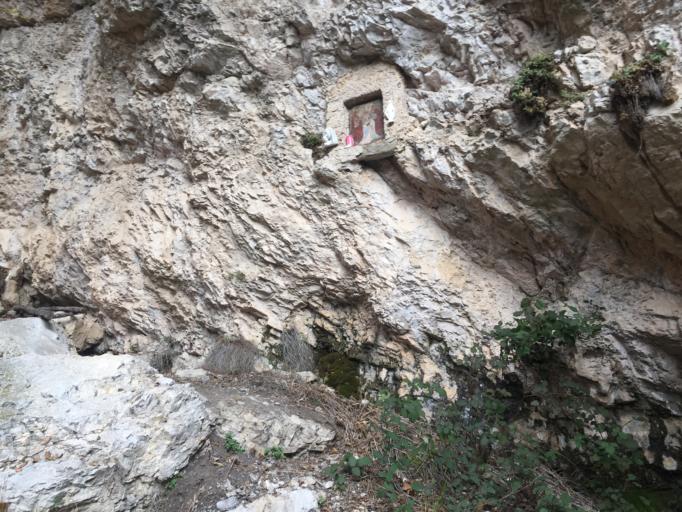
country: IT
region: Friuli Venezia Giulia
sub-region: Provincia di Udine
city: Chiusaforte
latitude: 46.4115
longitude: 13.2986
